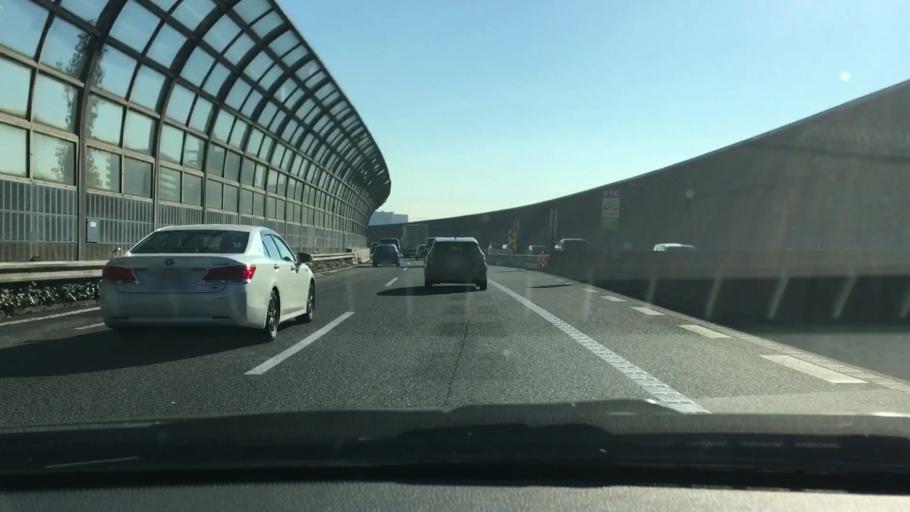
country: JP
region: Chiba
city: Funabashi
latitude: 35.6945
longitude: 139.9765
